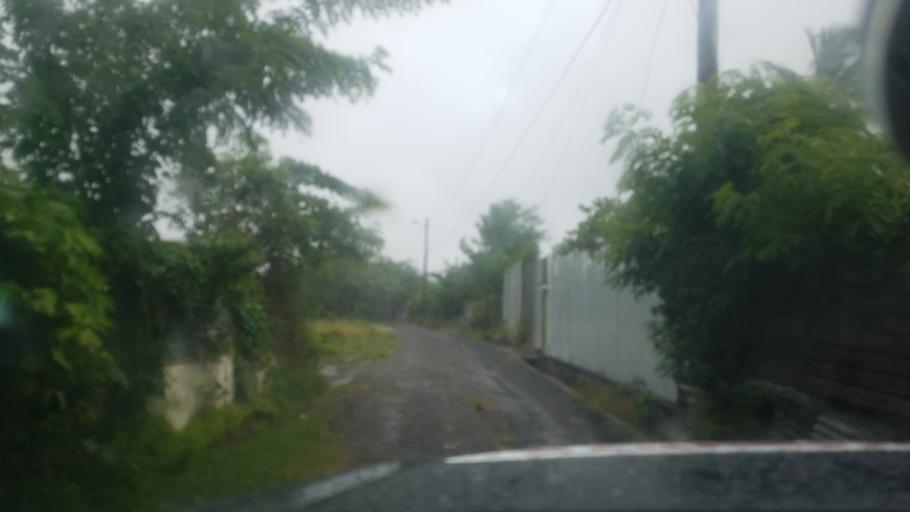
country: LC
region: Laborie Quarter
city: Laborie
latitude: 13.7602
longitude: -60.9776
